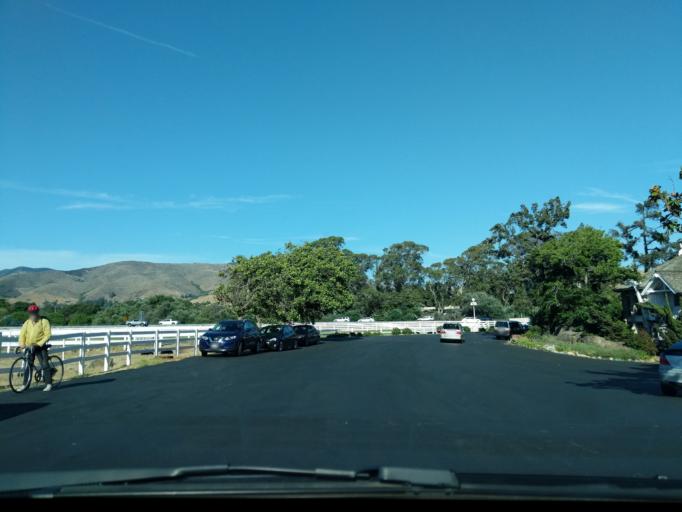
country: US
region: California
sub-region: San Luis Obispo County
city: San Luis Obispo
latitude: 35.2678
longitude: -120.6748
